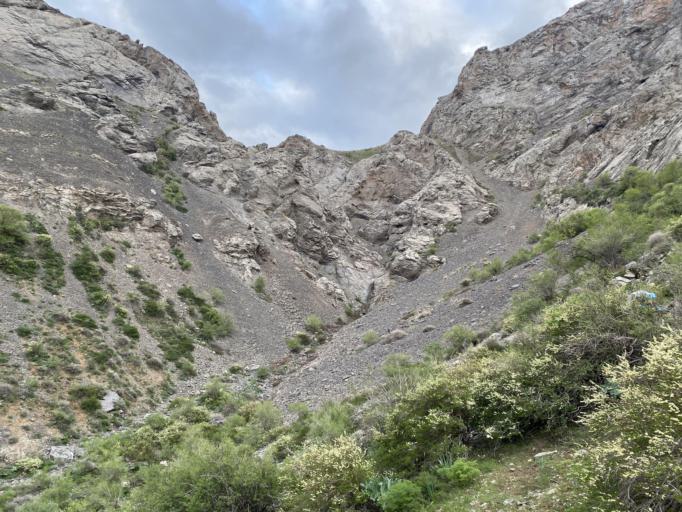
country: KZ
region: Ongtustik Qazaqstan
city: Ashchysay
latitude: 43.6650
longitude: 68.8755
